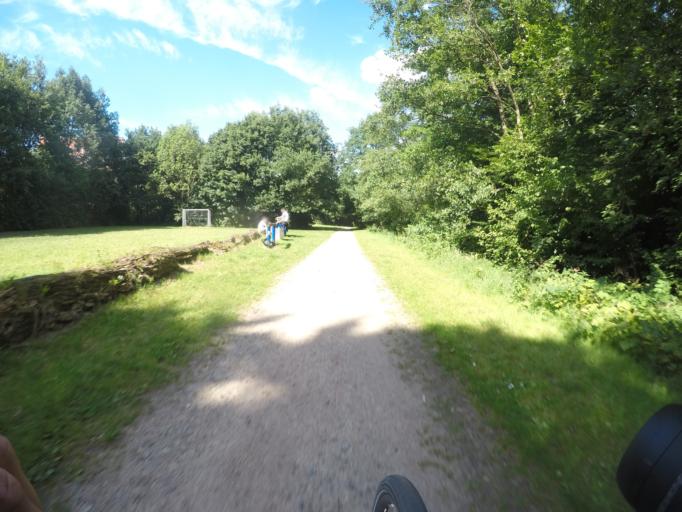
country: DE
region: Hamburg
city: Wandsbek
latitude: 53.5612
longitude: 10.1234
